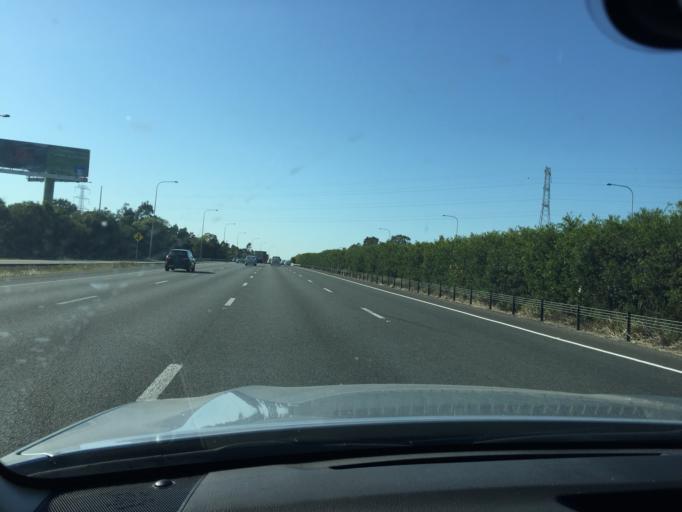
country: AU
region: Queensland
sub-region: Gold Coast
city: Yatala
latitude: -27.7211
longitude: 153.2150
